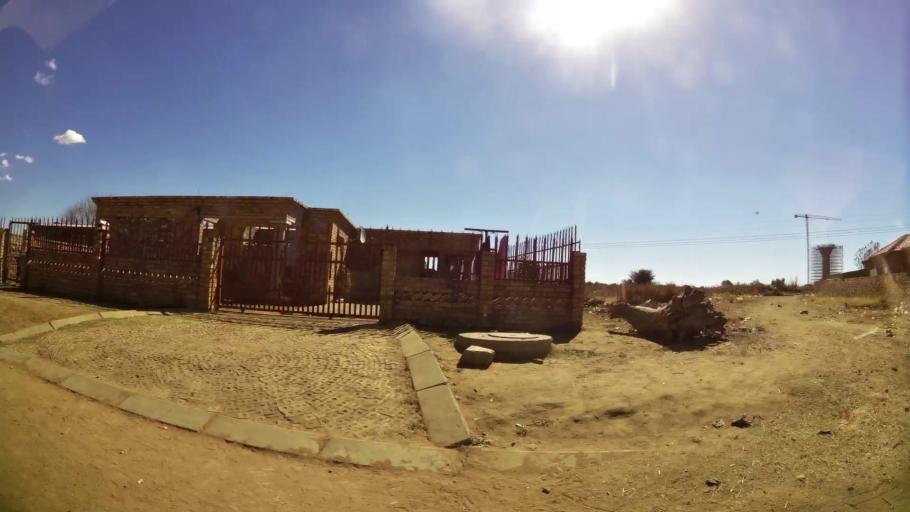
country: ZA
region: North-West
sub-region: Dr Kenneth Kaunda District Municipality
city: Klerksdorp
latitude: -26.8666
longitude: 26.5761
